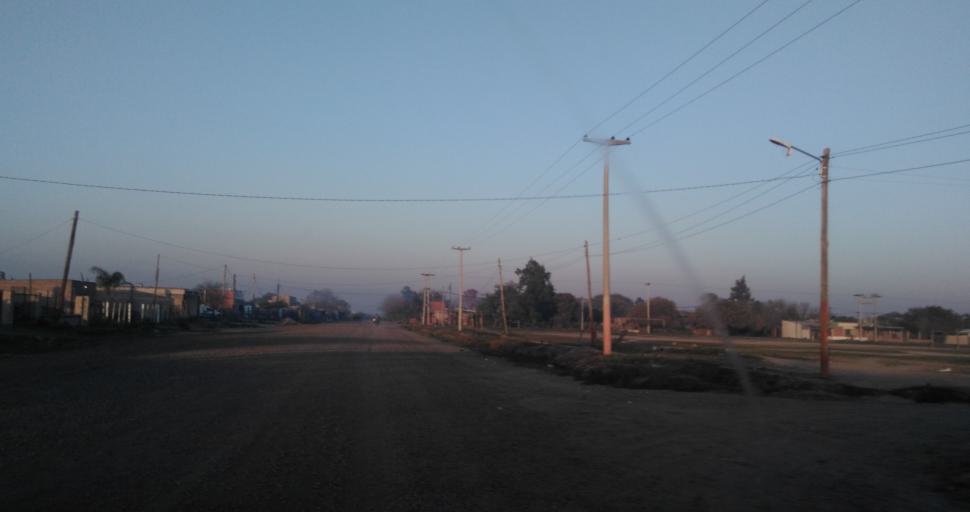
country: AR
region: Chaco
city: Resistencia
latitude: -27.4870
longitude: -58.9980
